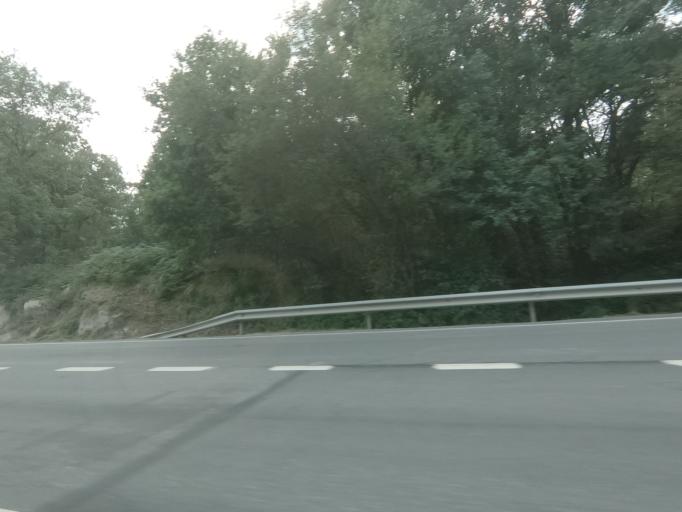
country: ES
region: Galicia
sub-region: Provincia de Ourense
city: Taboadela
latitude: 42.2422
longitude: -7.8435
